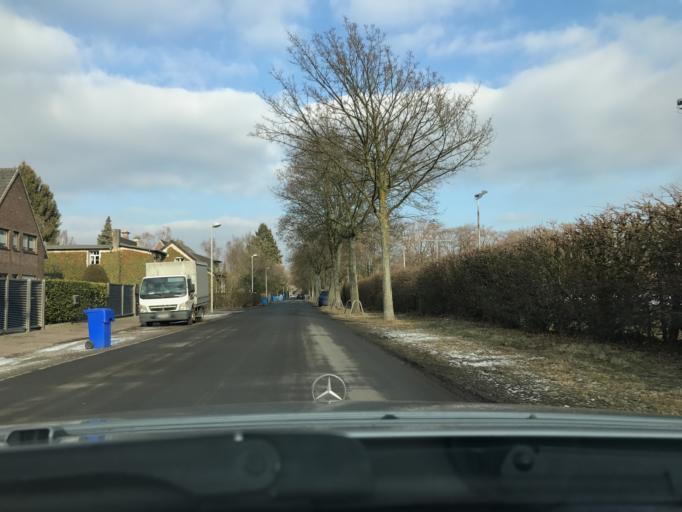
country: DE
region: North Rhine-Westphalia
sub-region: Regierungsbezirk Dusseldorf
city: Krefeld
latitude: 51.3514
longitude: 6.5697
